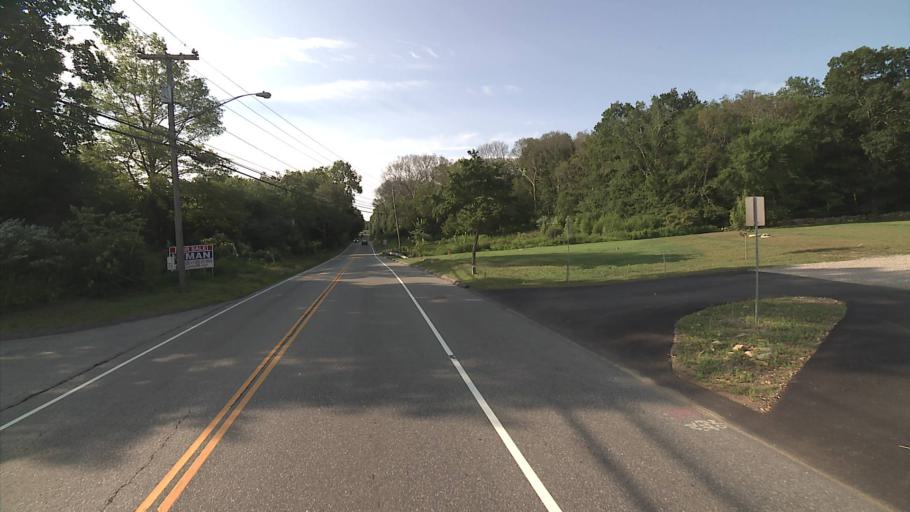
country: US
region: Connecticut
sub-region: New London County
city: Pawcatuck
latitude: 41.4226
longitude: -71.8595
